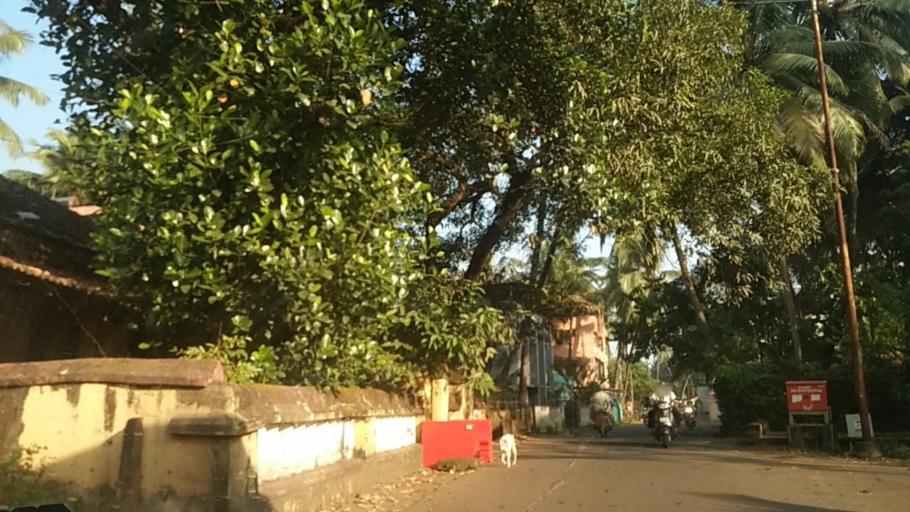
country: IN
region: Goa
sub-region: South Goa
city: Madgaon
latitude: 15.2805
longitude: 73.9560
